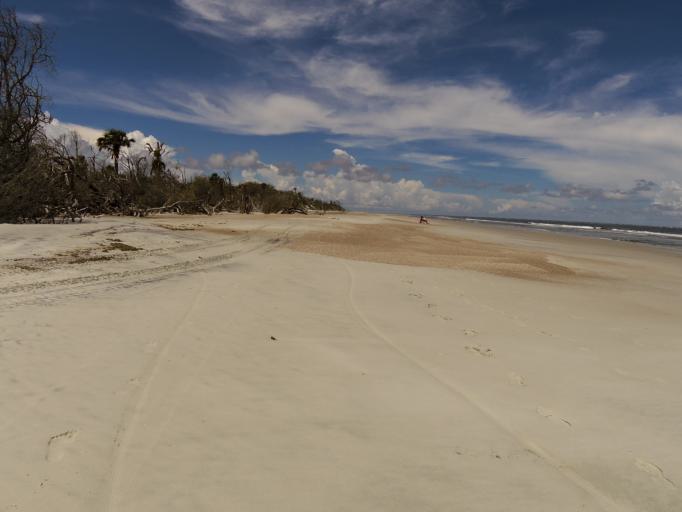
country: US
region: Florida
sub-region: Duval County
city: Atlantic Beach
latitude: 30.4740
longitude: -81.4132
